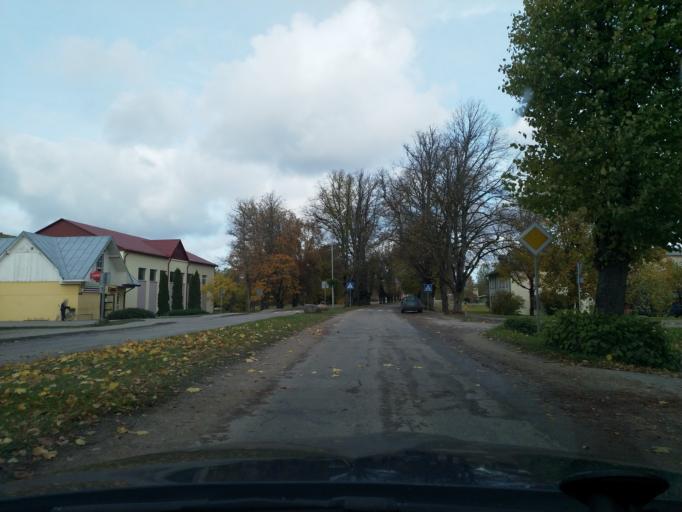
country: LV
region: Dundaga
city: Dundaga
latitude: 57.5064
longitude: 22.3500
